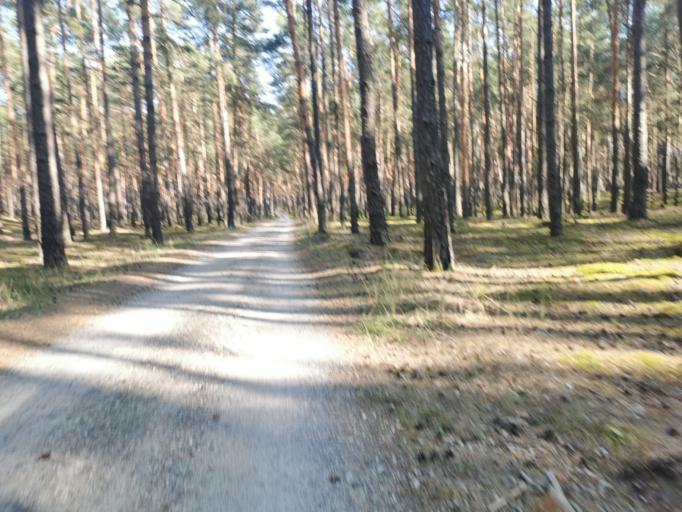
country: SK
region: Trnavsky
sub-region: Okres Senica
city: Senica
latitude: 48.6442
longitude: 17.2392
